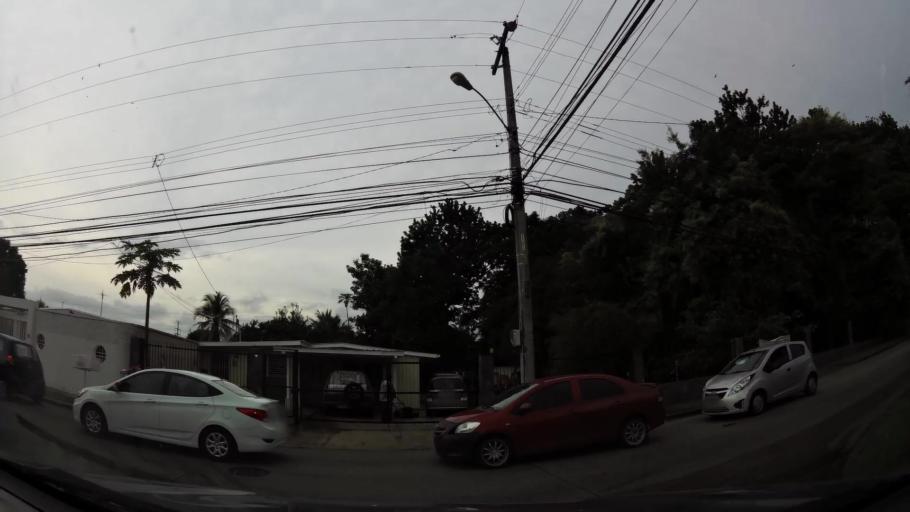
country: PA
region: Panama
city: Panama
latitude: 9.0115
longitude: -79.5407
